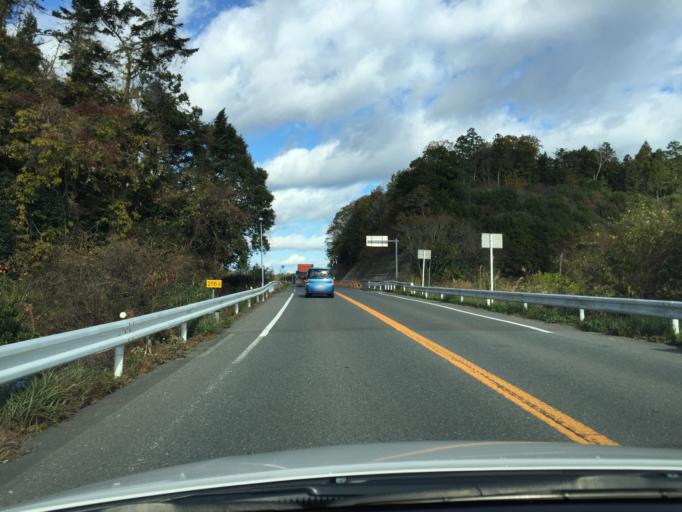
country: JP
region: Fukushima
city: Namie
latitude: 37.4596
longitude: 141.0104
